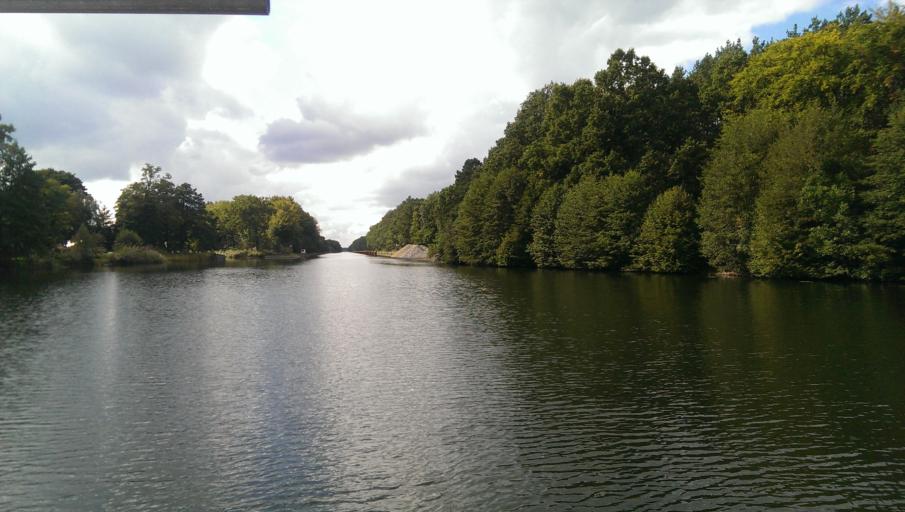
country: DE
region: Brandenburg
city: Marienwerder
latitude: 52.8511
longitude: 13.6080
